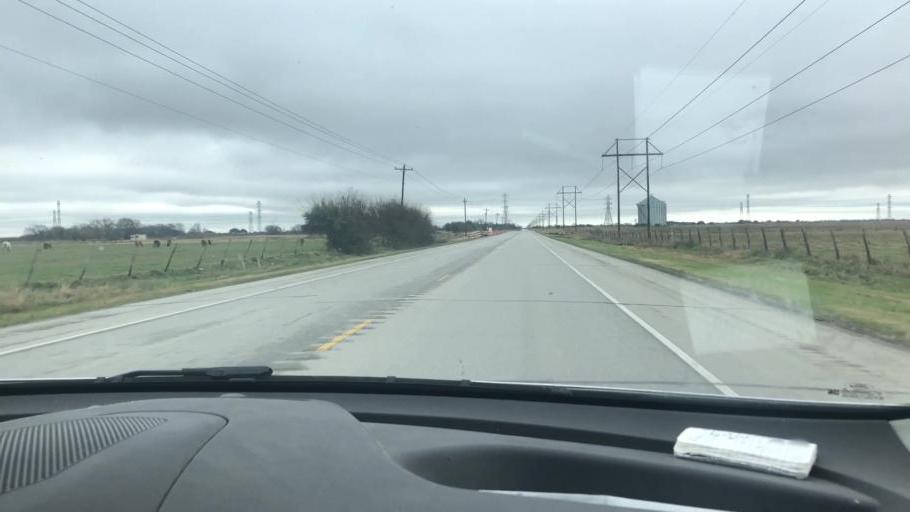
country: US
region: Texas
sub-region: Wharton County
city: Boling
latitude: 29.1830
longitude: -96.0098
